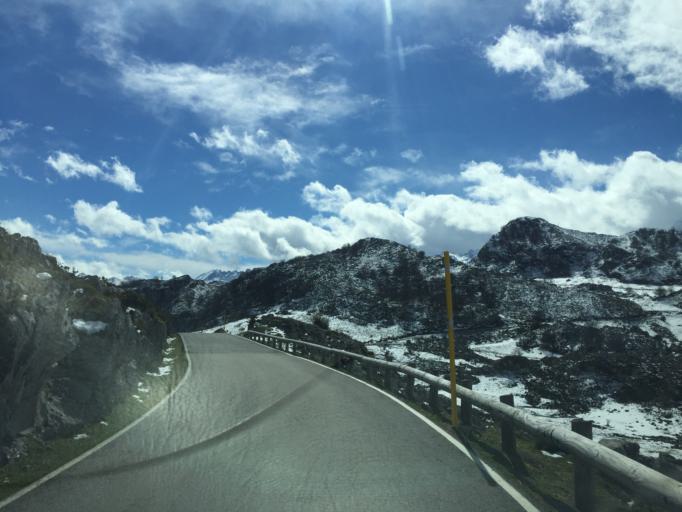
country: ES
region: Asturias
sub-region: Province of Asturias
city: Amieva
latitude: 43.2838
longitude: -5.0073
